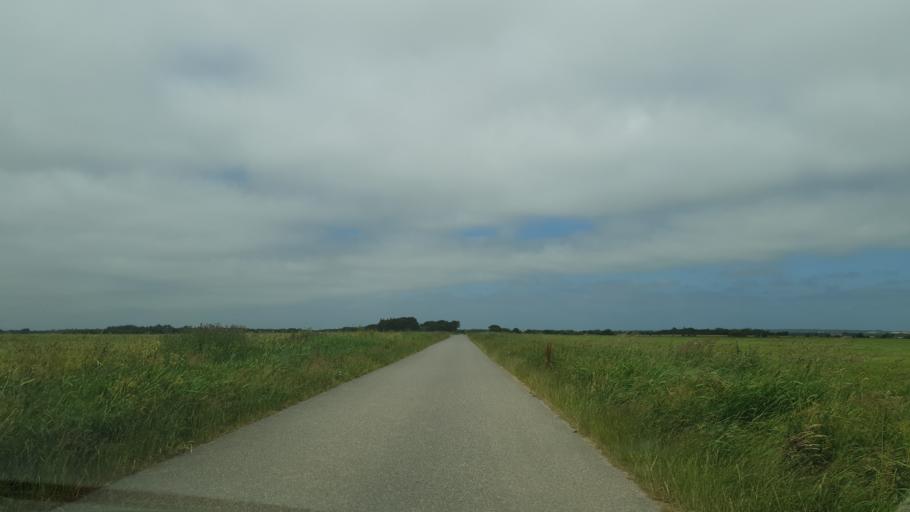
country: DK
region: Central Jutland
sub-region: Ringkobing-Skjern Kommune
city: Skjern
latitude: 55.9278
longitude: 8.4027
